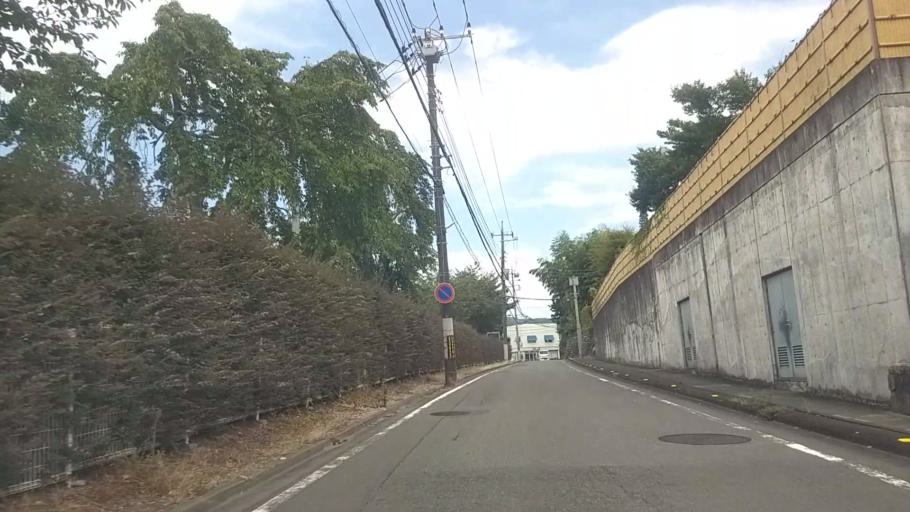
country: JP
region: Shizuoka
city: Mishima
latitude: 34.9893
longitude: 138.9418
